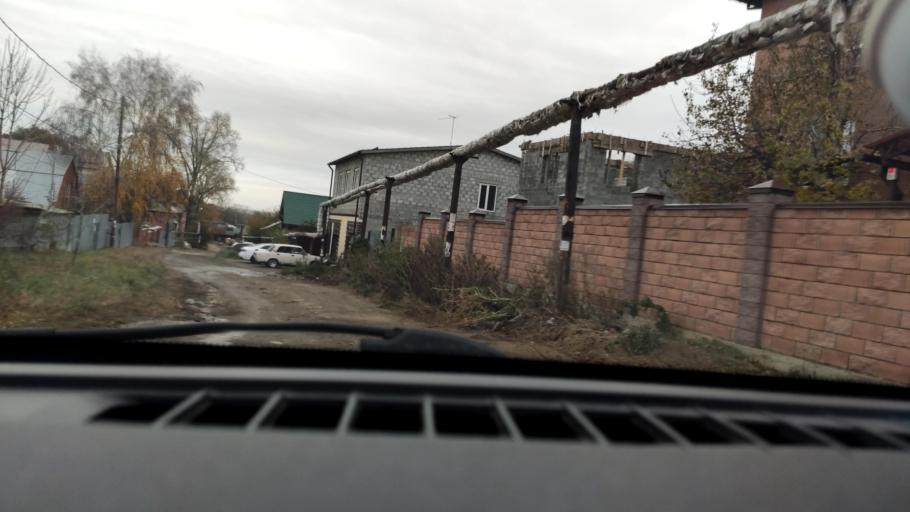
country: RU
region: Samara
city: Samara
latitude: 53.1846
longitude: 50.2083
